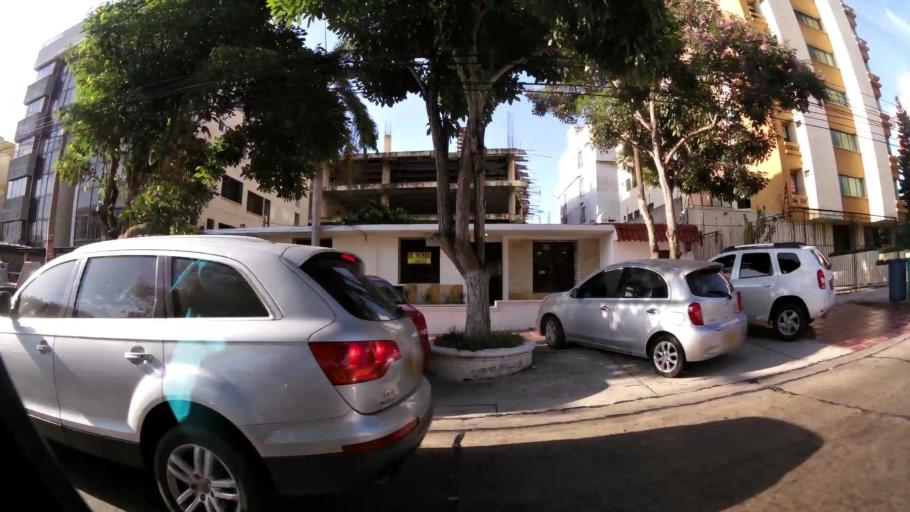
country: CO
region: Atlantico
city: Barranquilla
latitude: 11.0004
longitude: -74.8118
